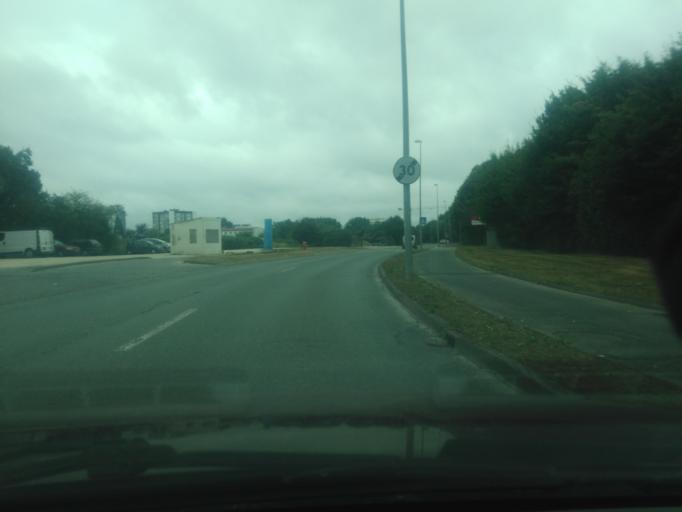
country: FR
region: Pays de la Loire
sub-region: Departement de la Vendee
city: La Roche-sur-Yon
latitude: 46.6847
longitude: -1.4338
